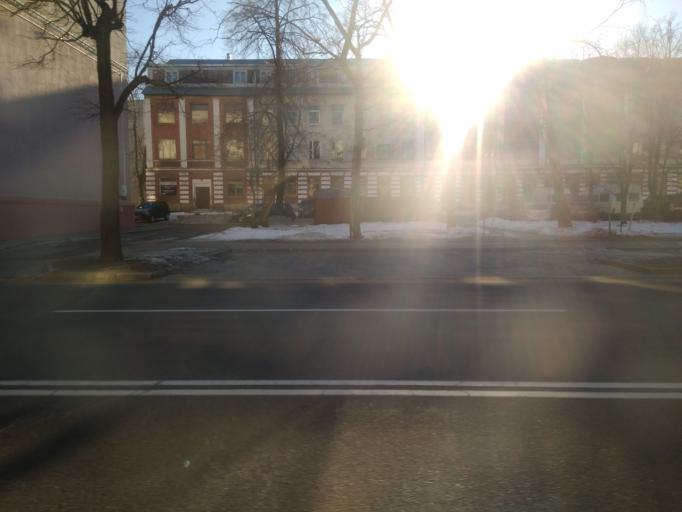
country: BY
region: Minsk
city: Minsk
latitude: 53.9042
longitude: 27.5810
